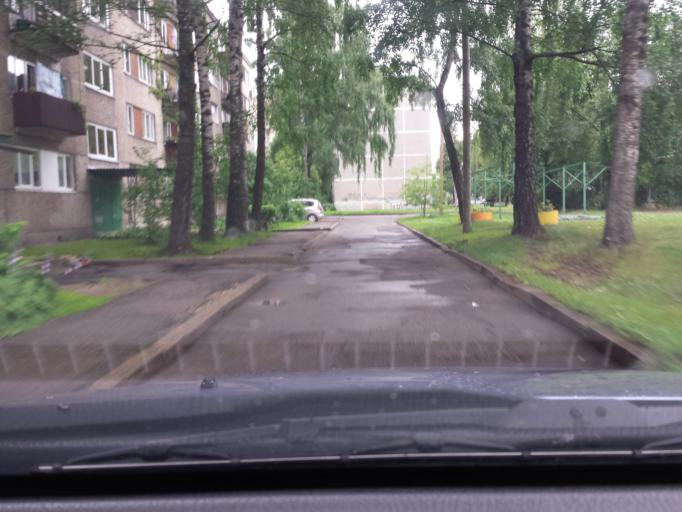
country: LV
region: Kekava
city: Kekava
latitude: 56.9029
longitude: 24.2033
